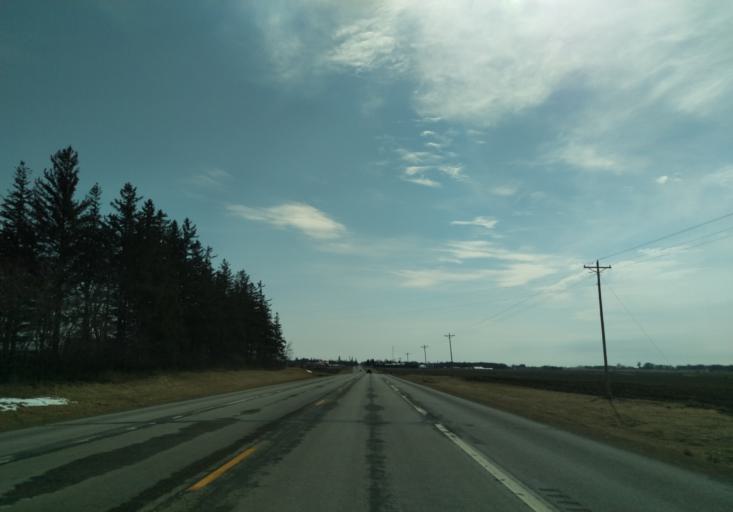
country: US
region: Minnesota
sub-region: Fillmore County
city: Harmony
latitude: 43.5771
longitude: -92.0098
